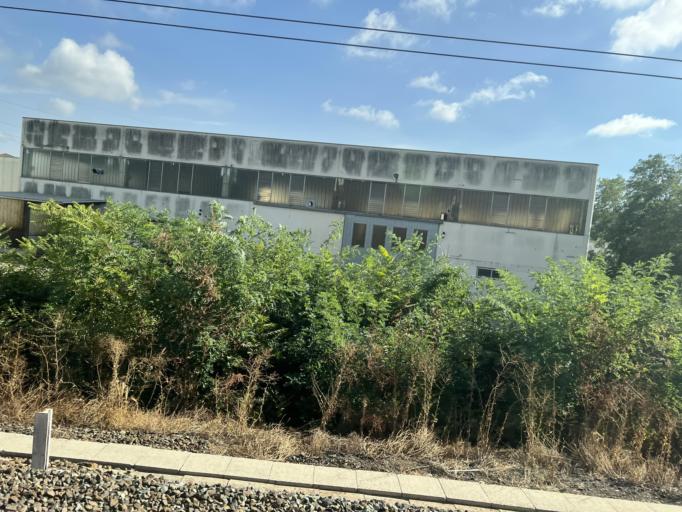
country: IT
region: Emilia-Romagna
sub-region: Provincia di Parma
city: Parma
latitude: 44.8137
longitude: 10.3082
